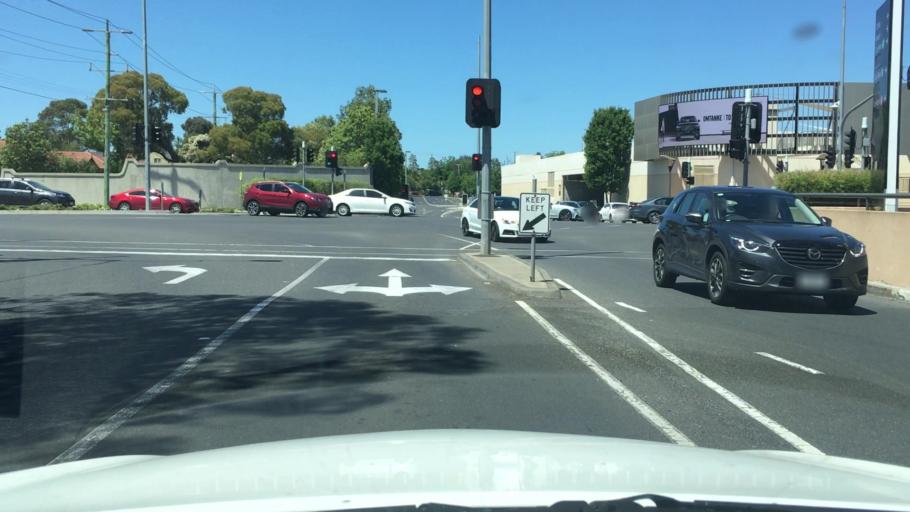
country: AU
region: Victoria
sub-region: Monash
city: Chadstone
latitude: -37.8863
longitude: 145.0863
